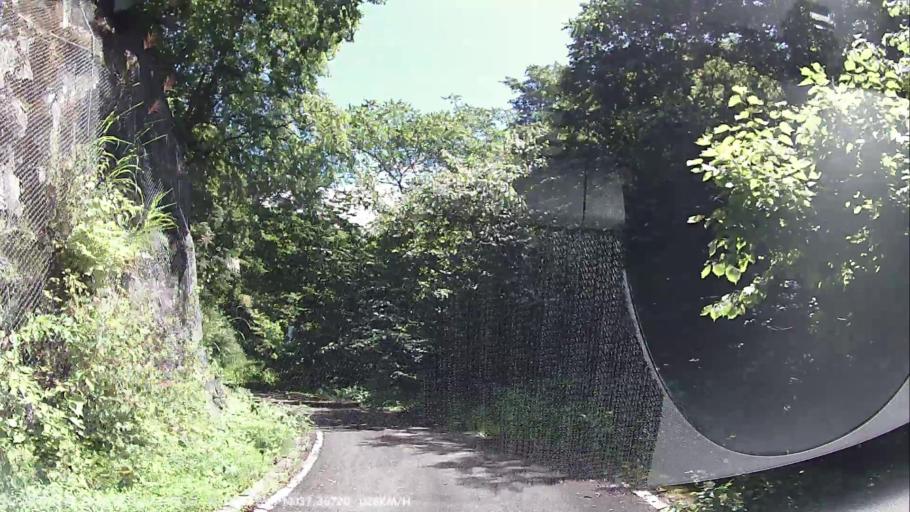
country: JP
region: Fukushima
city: Kitakata
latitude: 37.3672
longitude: 139.8613
